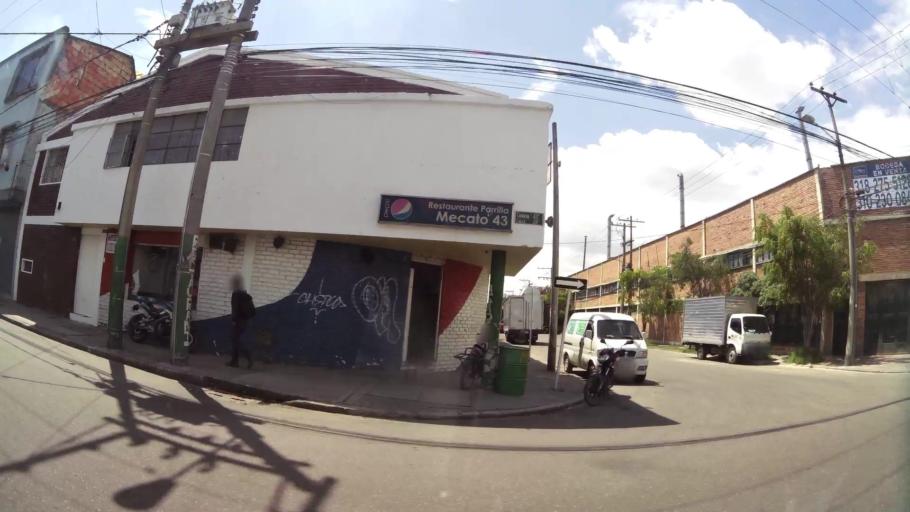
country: CO
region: Bogota D.C.
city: Bogota
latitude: 4.6287
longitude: -74.0981
